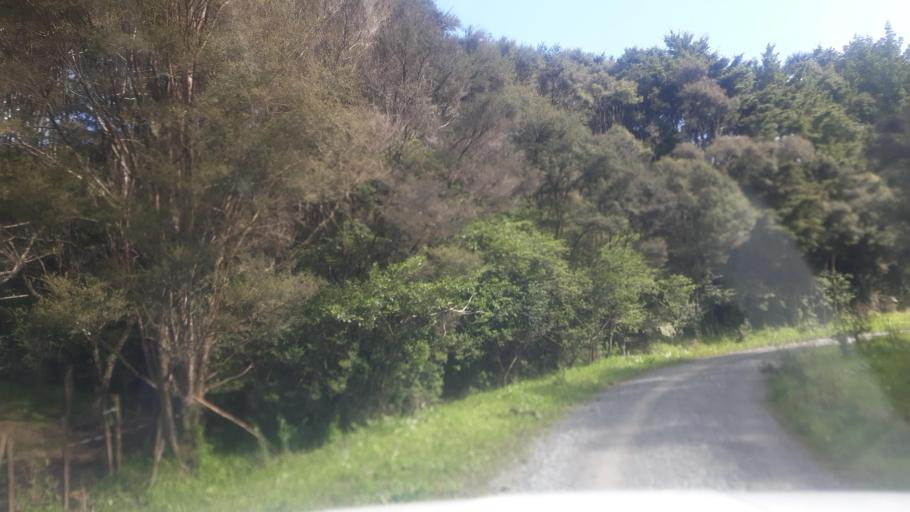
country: NZ
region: Northland
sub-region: Far North District
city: Taipa
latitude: -35.1184
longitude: 173.4338
